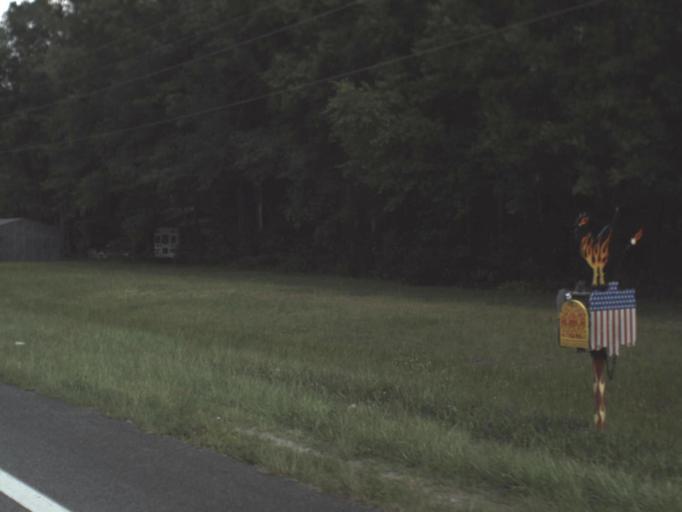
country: US
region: Florida
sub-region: Bradford County
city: Starke
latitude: 29.9538
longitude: -82.0744
